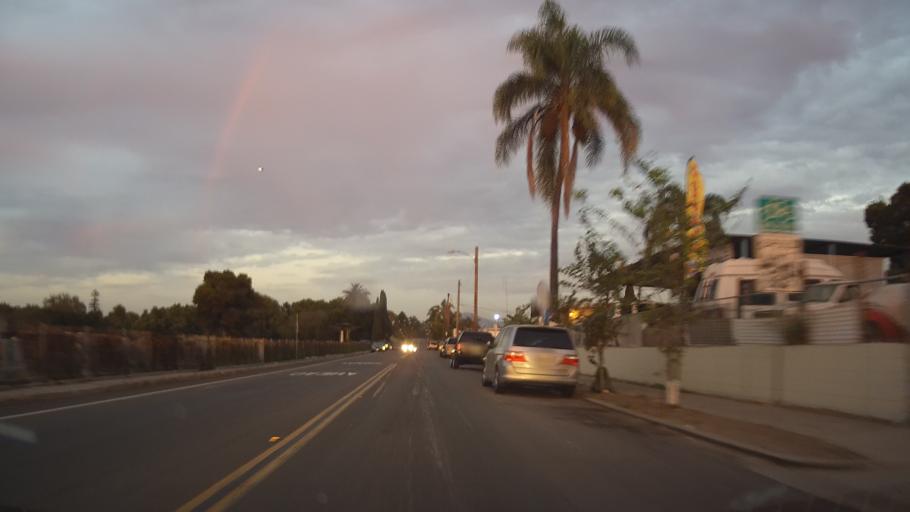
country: US
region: California
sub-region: San Diego County
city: National City
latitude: 32.7048
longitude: -117.1164
